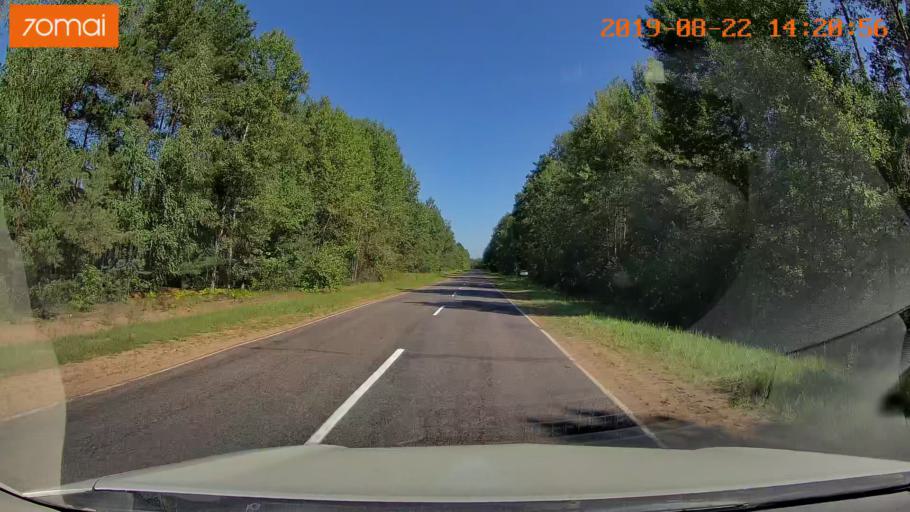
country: BY
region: Mogilev
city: Asipovichy
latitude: 53.2657
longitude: 28.5404
